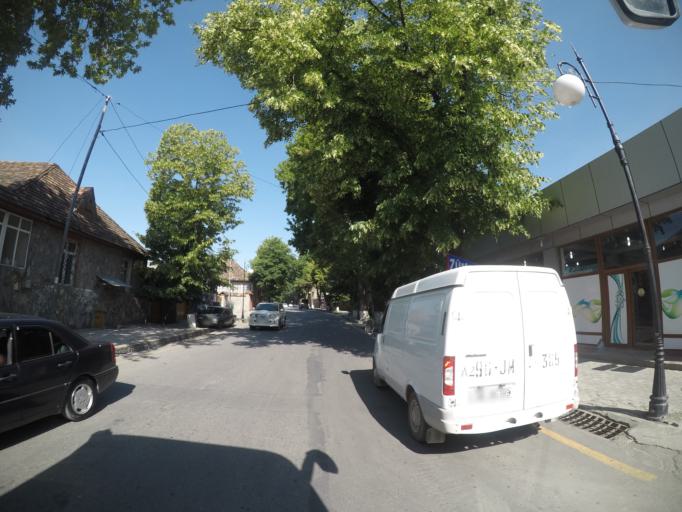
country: AZ
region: Shaki City
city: Sheki
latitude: 41.2056
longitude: 47.1759
